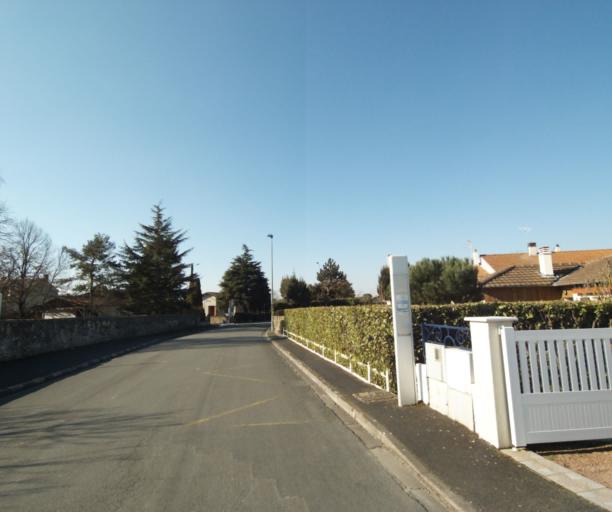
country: FR
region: Poitou-Charentes
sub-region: Departement des Deux-Sevres
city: Niort
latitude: 46.3312
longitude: -0.4238
